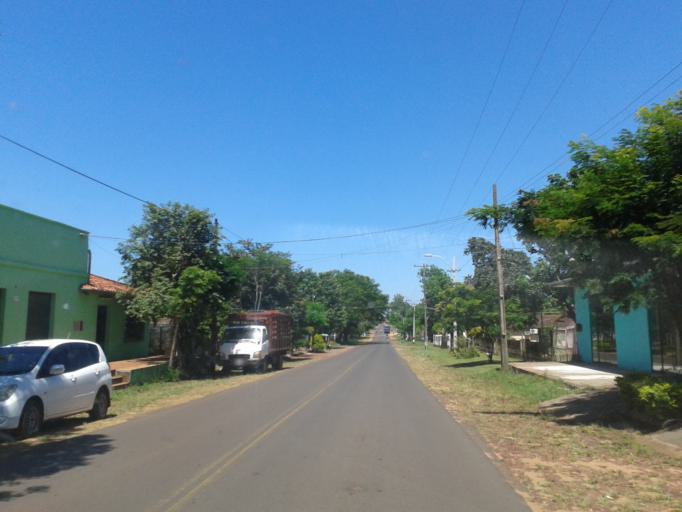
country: PY
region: Misiones
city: Santa Rosa
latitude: -26.8877
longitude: -56.8546
